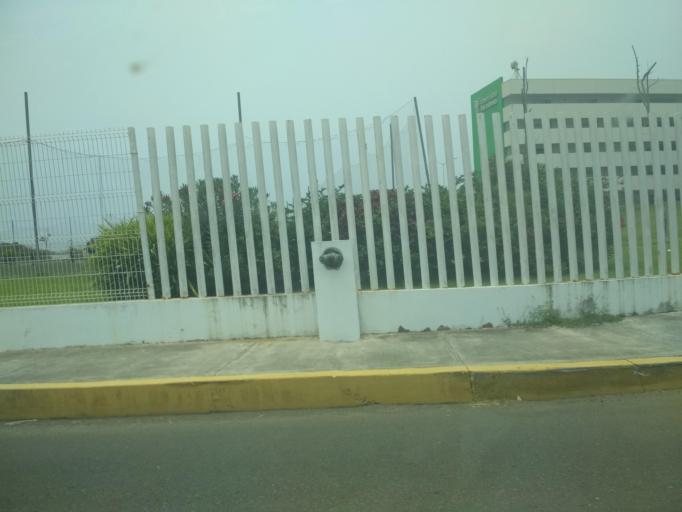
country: MX
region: Veracruz
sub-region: Alvarado
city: Playa de la Libertad
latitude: 19.0576
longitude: -96.0679
